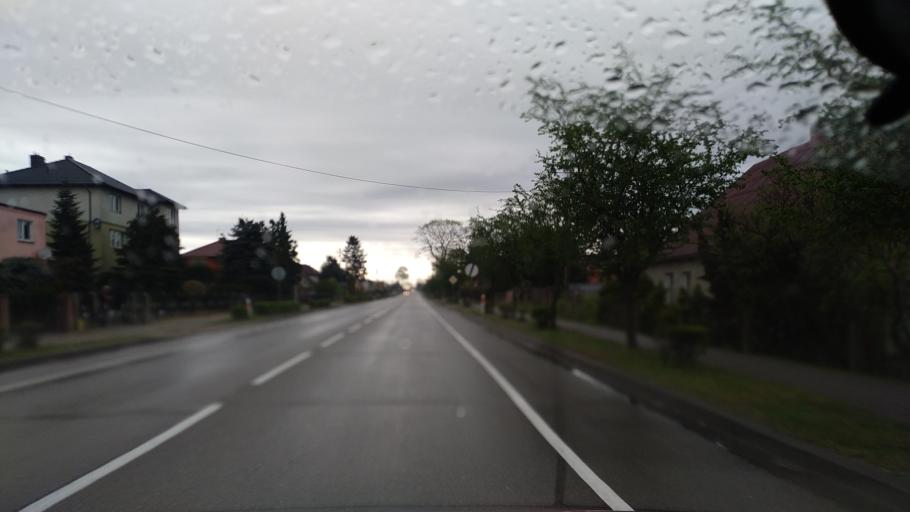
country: PL
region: Pomeranian Voivodeship
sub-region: Powiat chojnicki
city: Czersk
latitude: 53.7974
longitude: 17.9855
